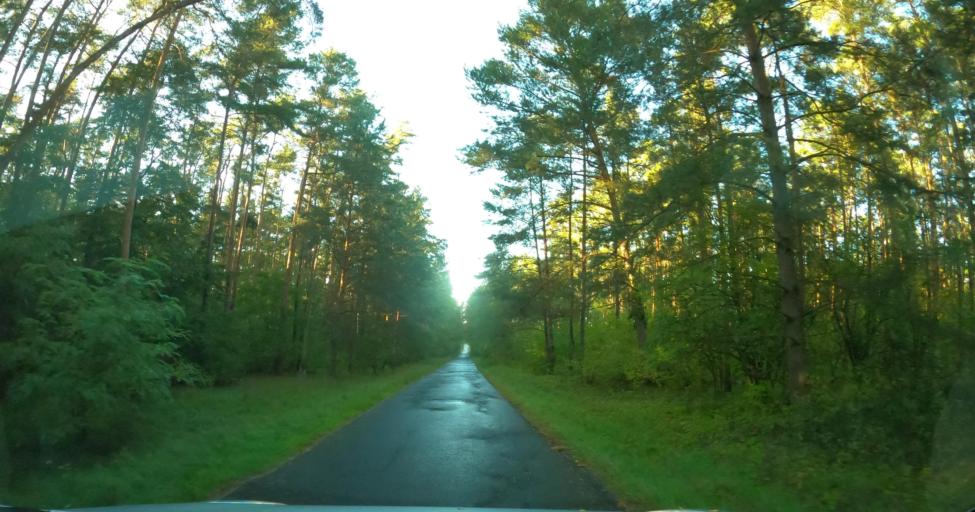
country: PL
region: Lubusz
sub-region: Powiat zielonogorski
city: Zabor
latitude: 51.9602
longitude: 15.6880
